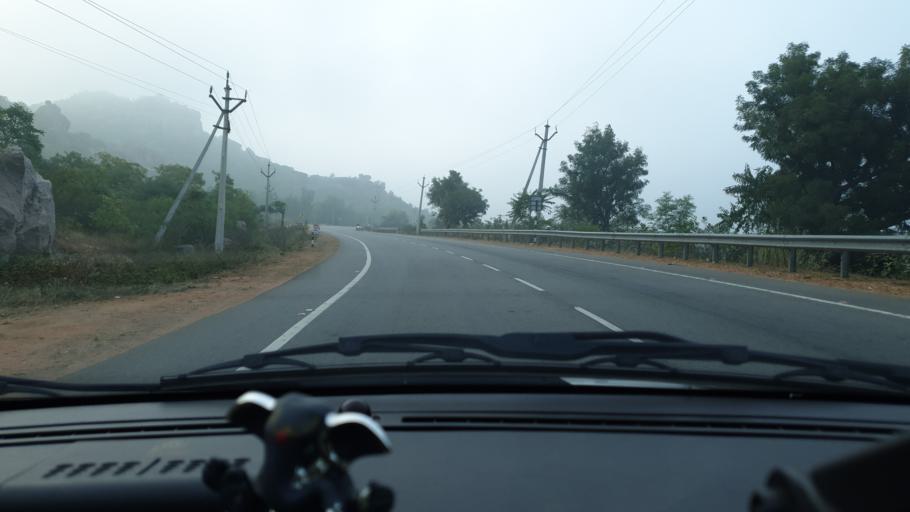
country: IN
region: Telangana
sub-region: Mahbubnagar
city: Farrukhnagar
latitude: 16.8945
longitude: 78.5297
